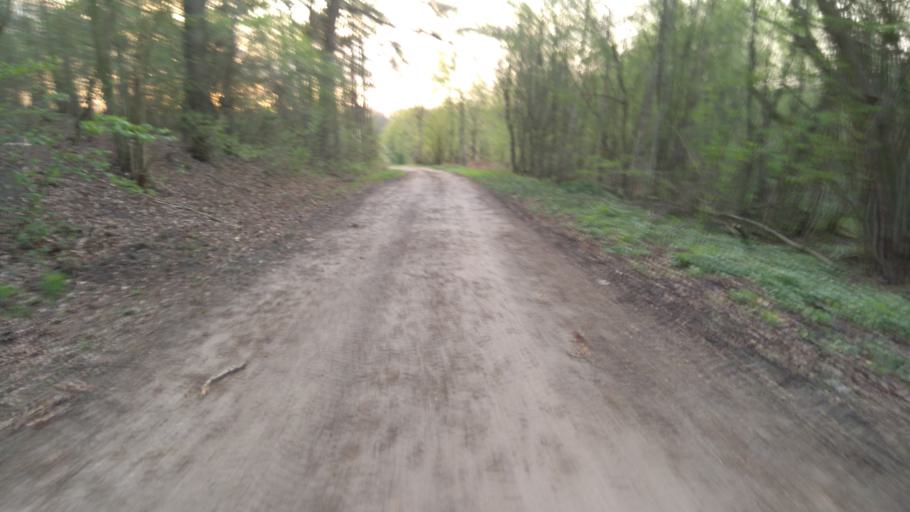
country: DE
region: Lower Saxony
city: Bliedersdorf
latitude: 53.4827
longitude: 9.5491
